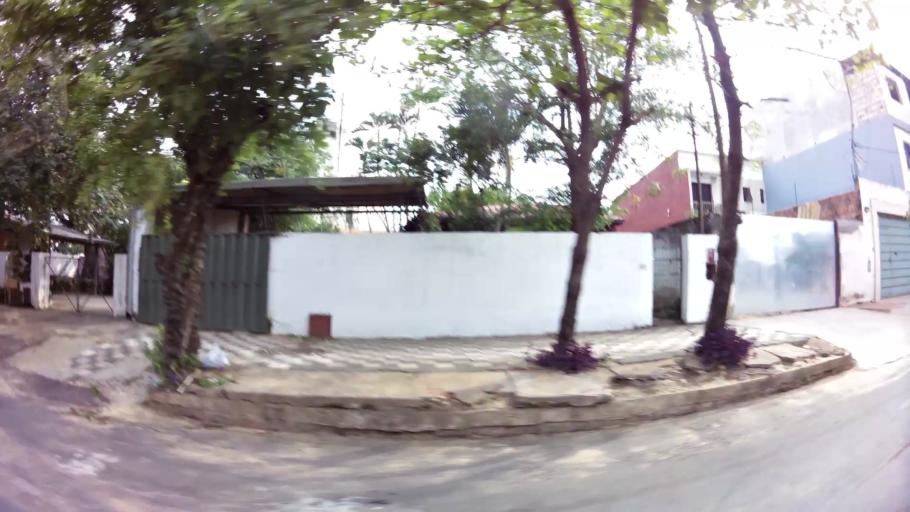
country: PY
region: Central
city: Fernando de la Mora
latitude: -25.3021
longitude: -57.5547
